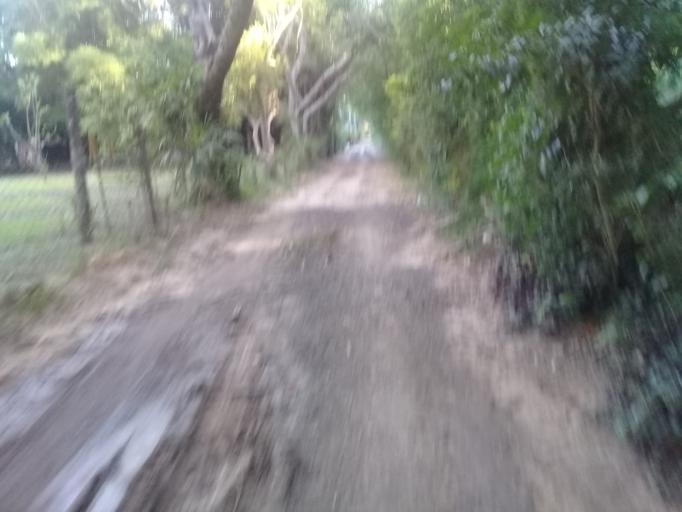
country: AR
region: Corrientes
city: San Luis del Palmar
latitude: -27.4612
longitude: -58.6633
